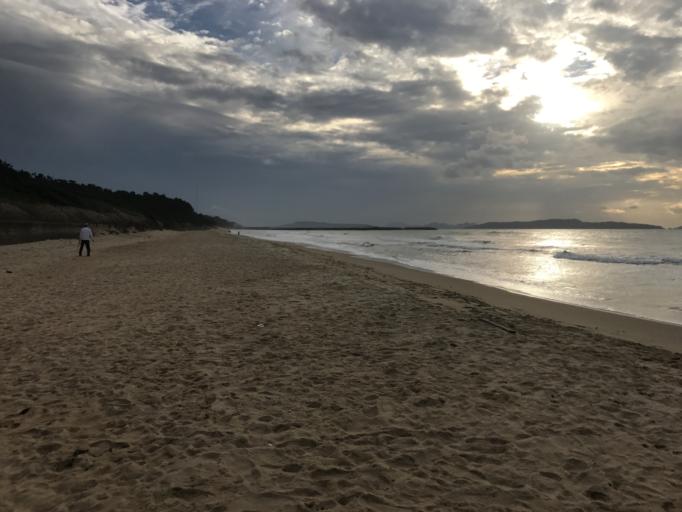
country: JP
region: Fukuoka
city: Shingu
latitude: 33.7023
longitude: 130.4160
